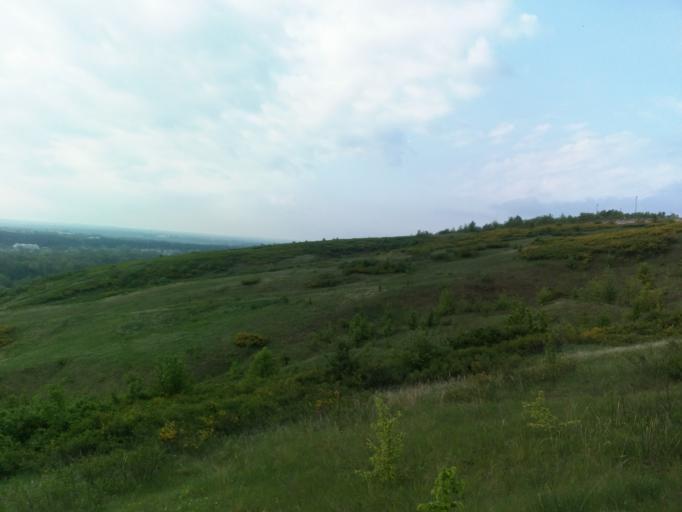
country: RU
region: Voronezj
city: Kalach
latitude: 50.4152
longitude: 41.0043
